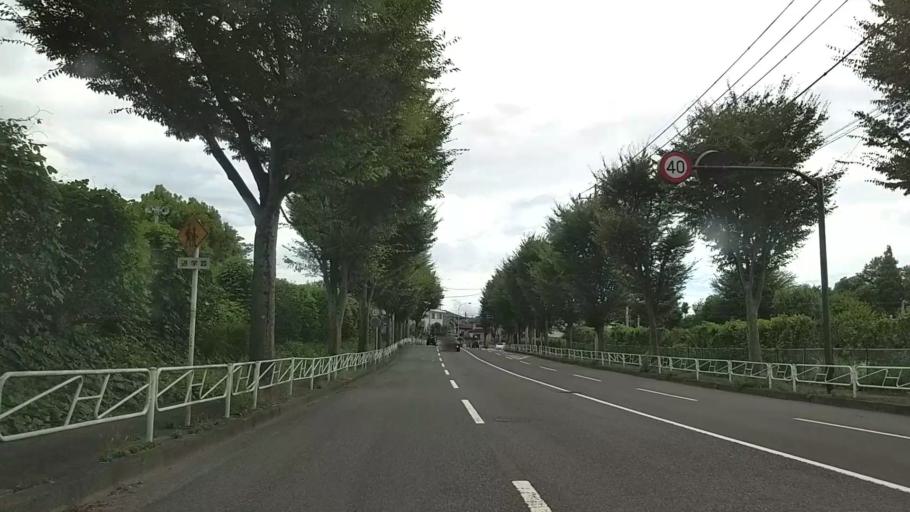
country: JP
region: Tokyo
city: Hachioji
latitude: 35.6363
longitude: 139.3568
